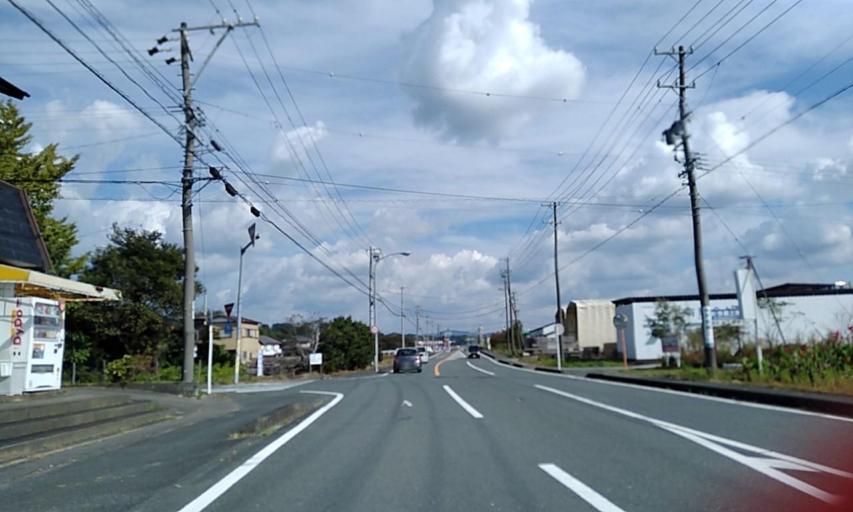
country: JP
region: Shizuoka
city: Mori
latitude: 34.8212
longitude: 137.8843
